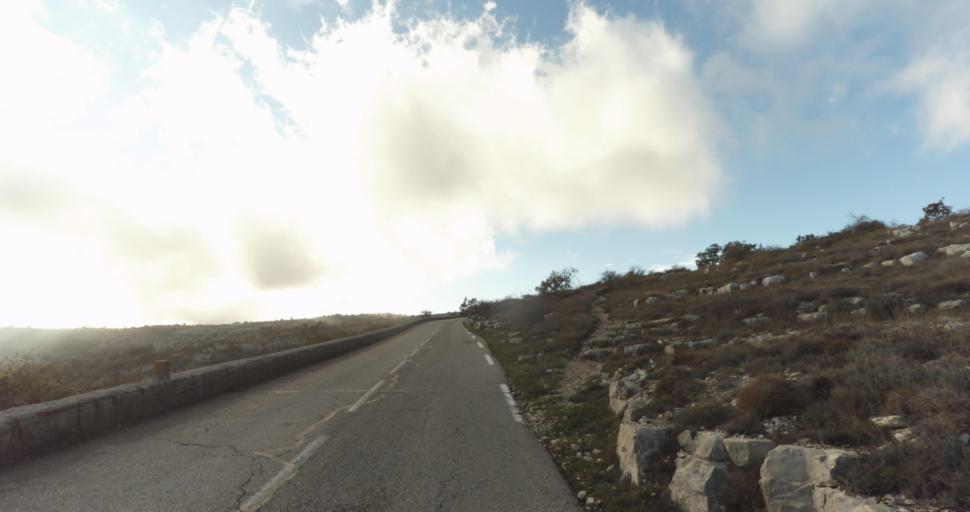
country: FR
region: Provence-Alpes-Cote d'Azur
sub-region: Departement des Alpes-Maritimes
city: Vence
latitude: 43.7568
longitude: 7.0794
